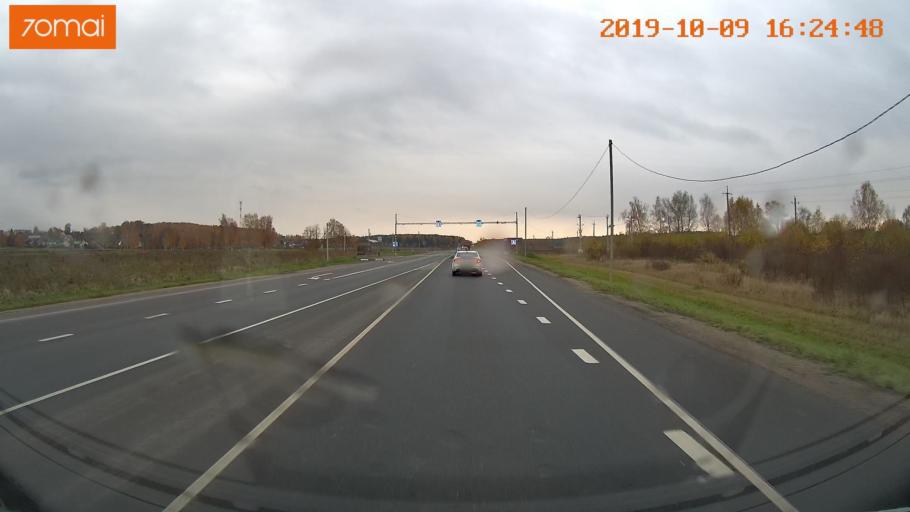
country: RU
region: Kostroma
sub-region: Kostromskoy Rayon
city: Kostroma
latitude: 57.6484
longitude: 40.9141
